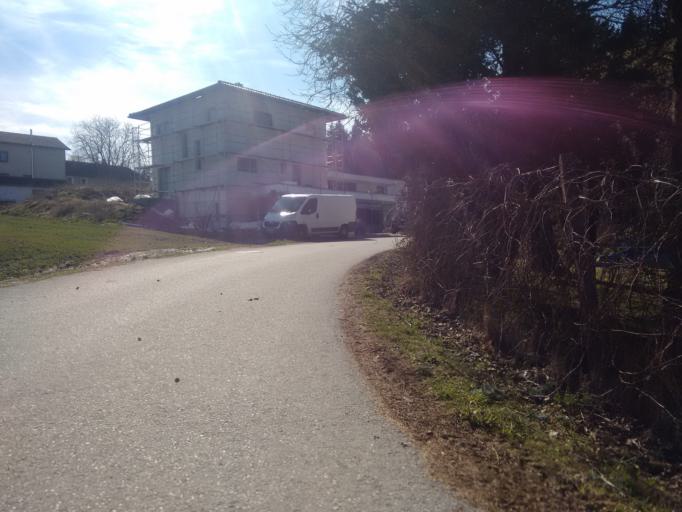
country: AT
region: Upper Austria
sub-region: Politischer Bezirk Grieskirchen
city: Bad Schallerbach
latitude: 48.2005
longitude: 13.9671
